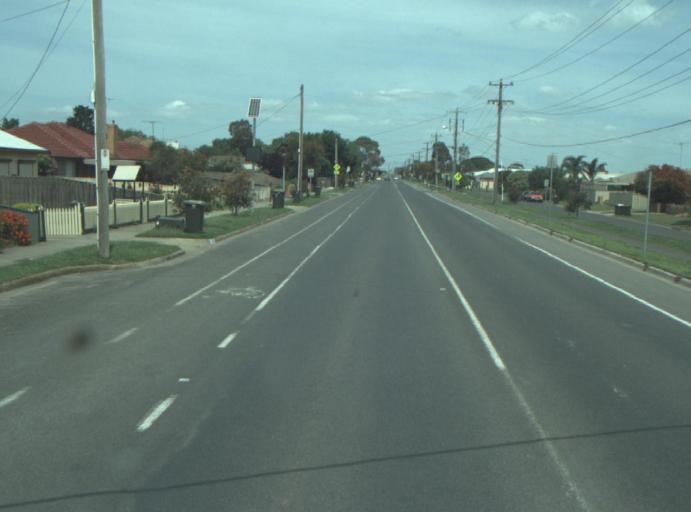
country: AU
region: Victoria
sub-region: Greater Geelong
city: Lara
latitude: -38.0285
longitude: 144.3954
